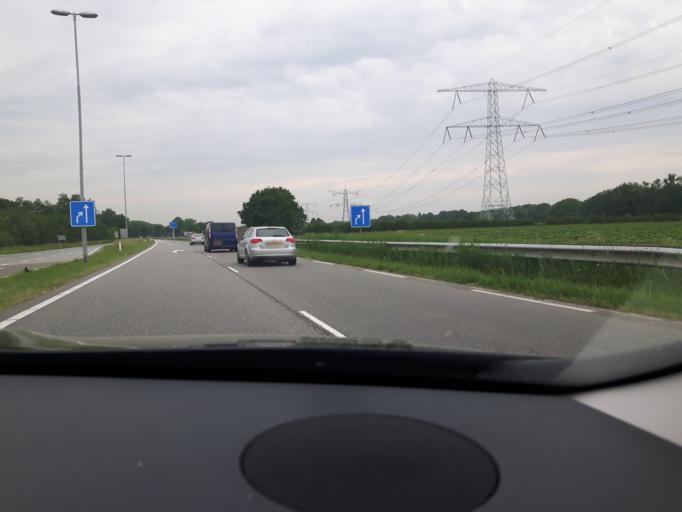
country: NL
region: North Brabant
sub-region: Gemeente Bergen op Zoom
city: Lepelstraat
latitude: 51.5431
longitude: 4.2845
